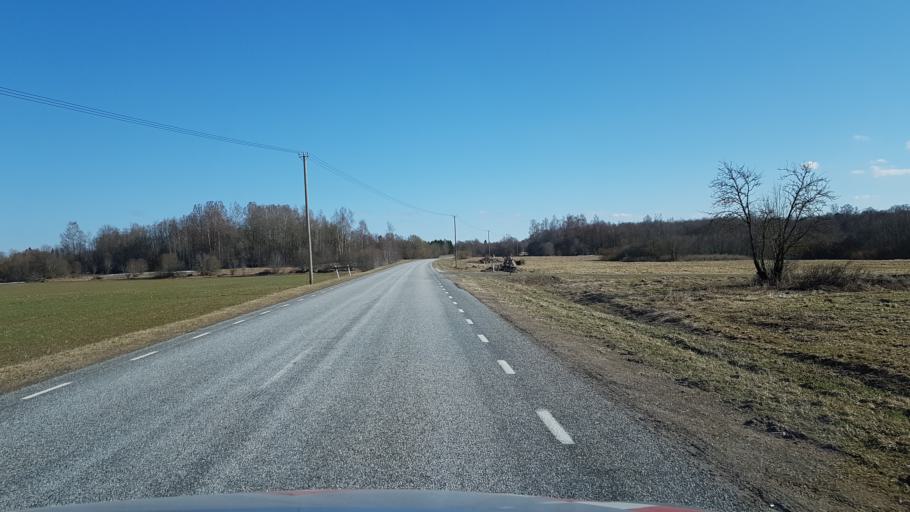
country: EE
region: Laeaene-Virumaa
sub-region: Haljala vald
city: Haljala
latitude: 59.4861
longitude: 26.1506
